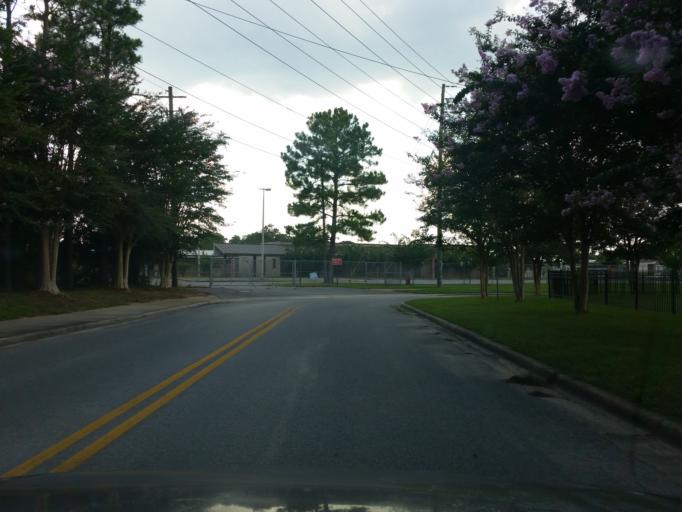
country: US
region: Florida
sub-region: Escambia County
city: Ferry Pass
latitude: 30.4854
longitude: -87.2051
